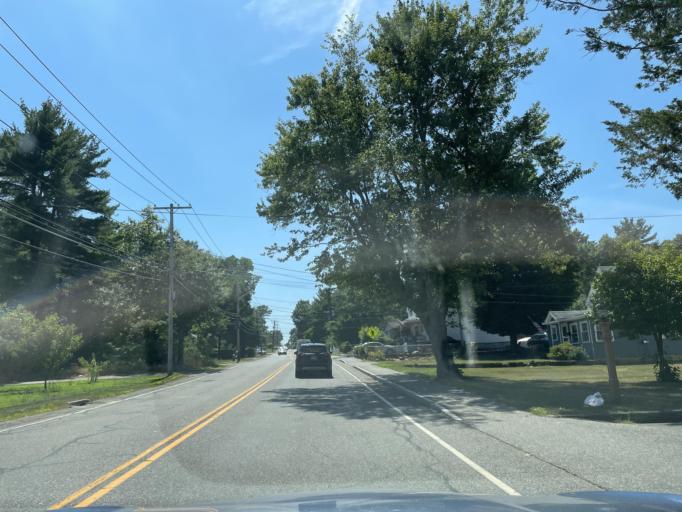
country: US
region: Massachusetts
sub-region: Norfolk County
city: Stoughton
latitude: 42.1359
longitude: -71.0878
